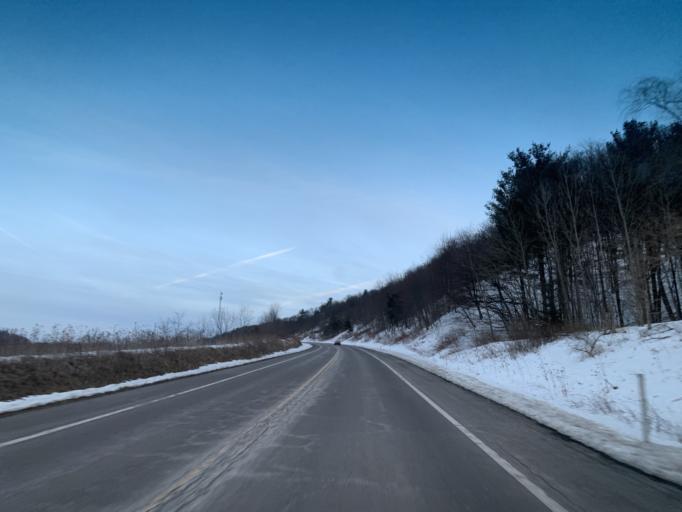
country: US
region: Maryland
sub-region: Allegany County
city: Cumberland
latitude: 39.6954
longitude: -78.6408
